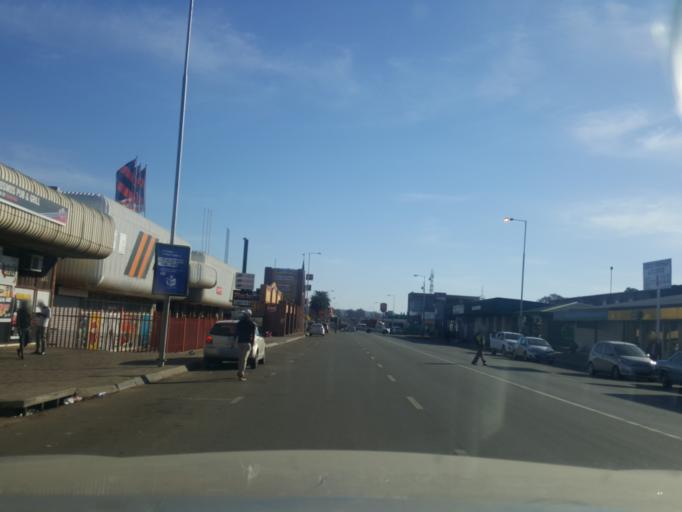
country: ZA
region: North-West
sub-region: Ngaka Modiri Molema District Municipality
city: Zeerust
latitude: -25.5440
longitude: 26.0845
